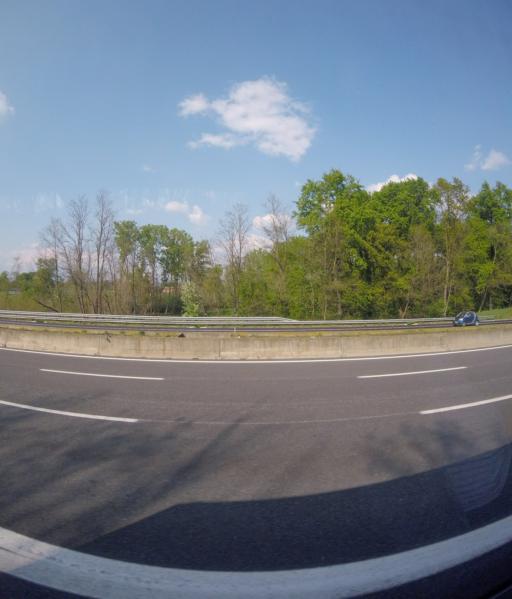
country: IT
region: Piedmont
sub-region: Provincia di Novara
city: Borgo Ticino
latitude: 45.7000
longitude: 8.6099
